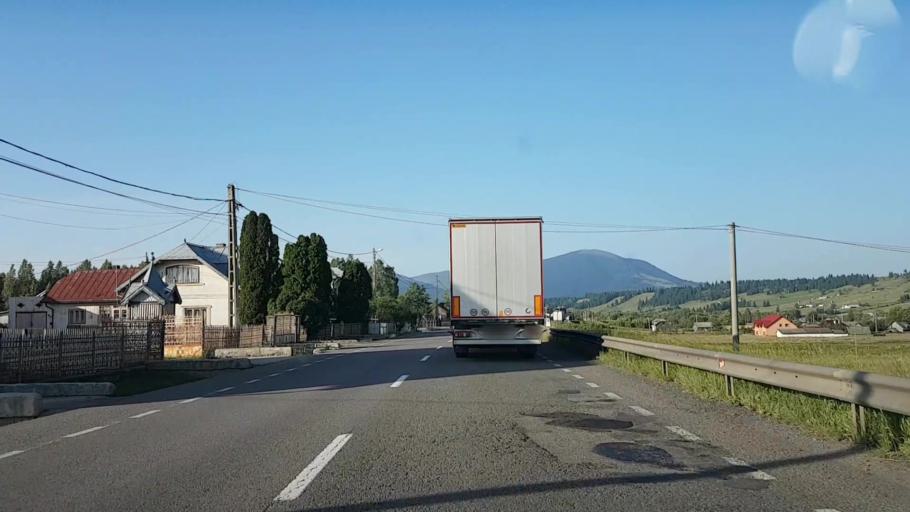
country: RO
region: Suceava
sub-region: Comuna Poiana Stampei
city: Poiana Stampei
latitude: 47.3310
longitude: 25.1549
